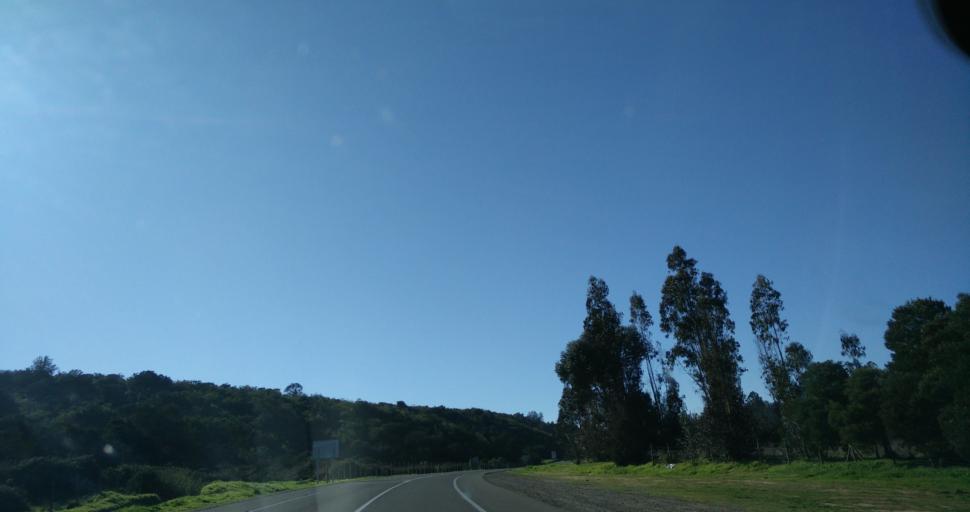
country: CL
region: Valparaiso
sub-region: San Antonio Province
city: Cartagena
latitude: -33.4265
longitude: -71.4487
